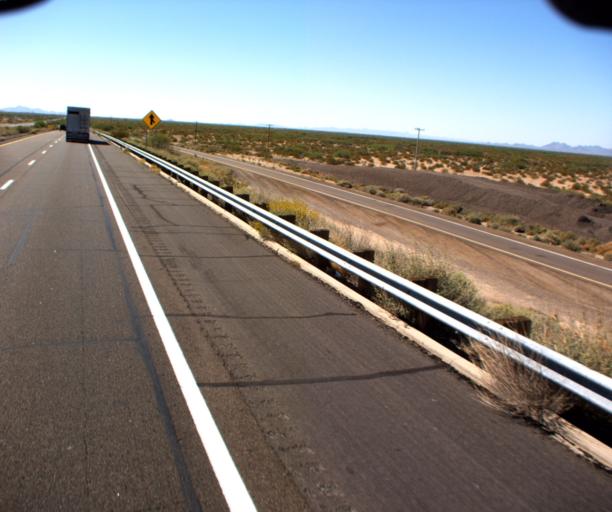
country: US
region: Arizona
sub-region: Maricopa County
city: Gila Bend
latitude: 32.8357
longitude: -113.3579
